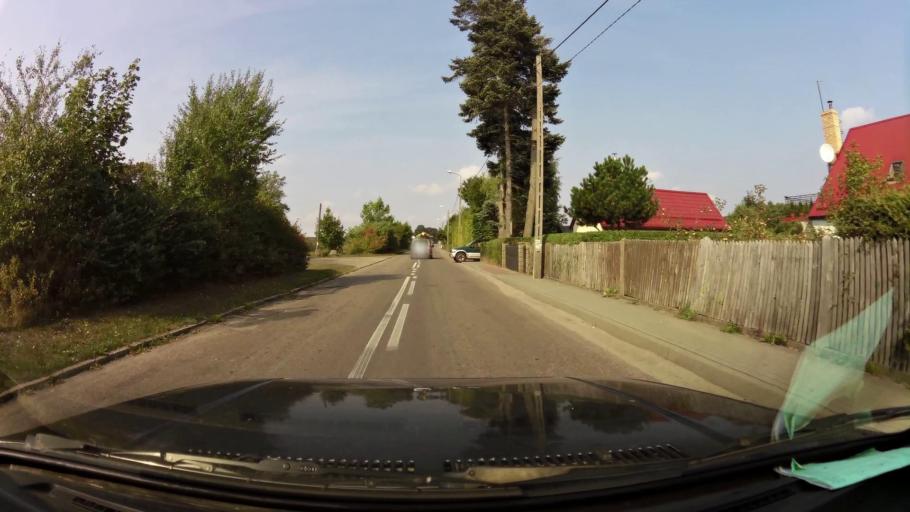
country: PL
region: West Pomeranian Voivodeship
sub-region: Powiat bialogardzki
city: Tychowo
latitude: 54.0692
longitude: 16.2982
